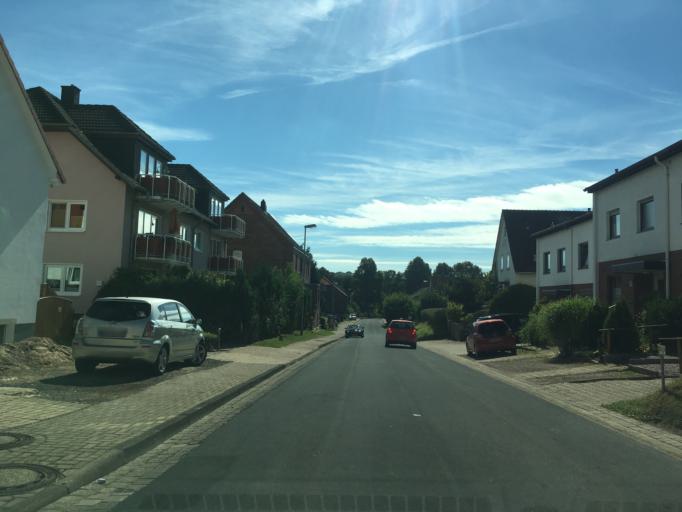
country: DE
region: Lower Saxony
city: Hameln
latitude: 52.0792
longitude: 9.3362
